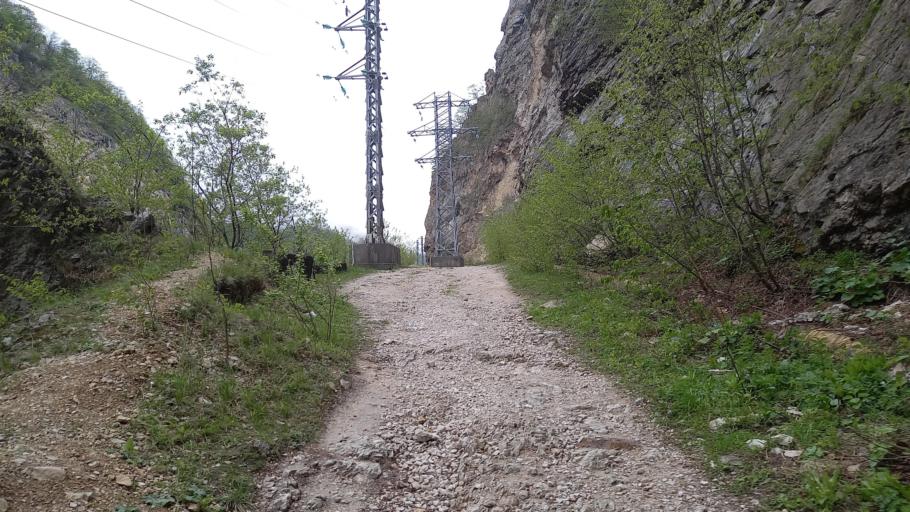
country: RU
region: Kabardino-Balkariya
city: Verkhnyaya Balkariya
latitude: 43.1884
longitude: 43.5165
